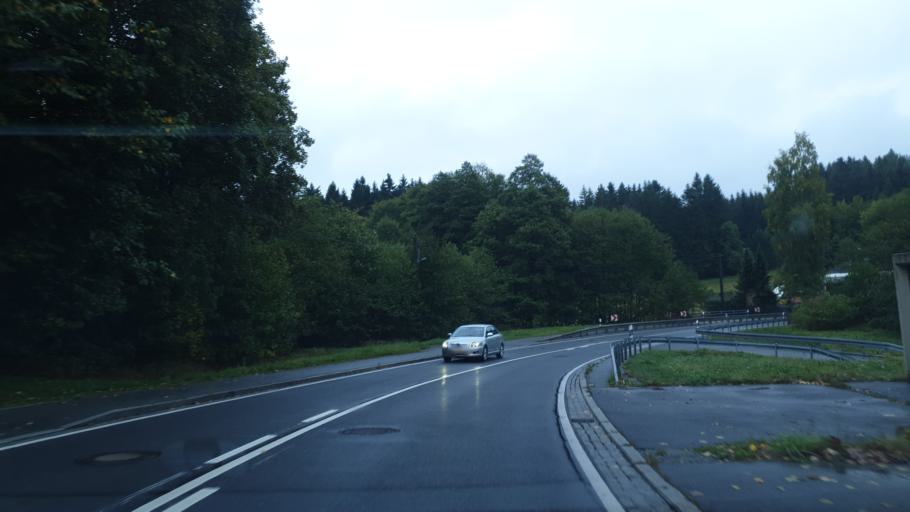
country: DE
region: Saxony
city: Neustadt Vogtland
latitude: 50.4466
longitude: 12.3328
